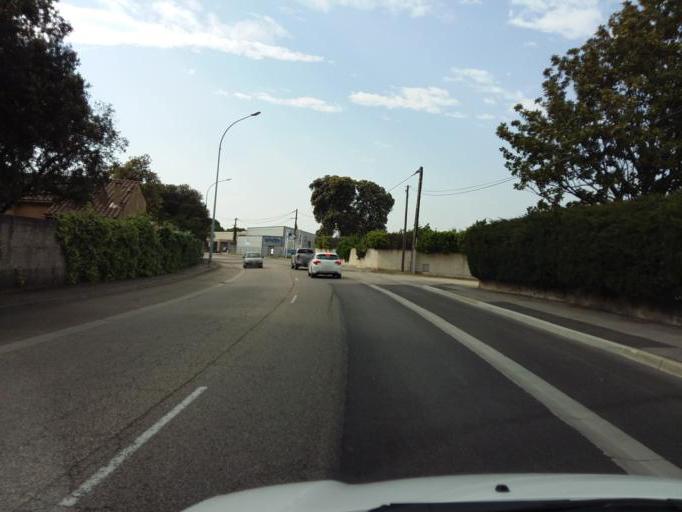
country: FR
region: Provence-Alpes-Cote d'Azur
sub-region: Departement du Vaucluse
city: Bollene
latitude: 44.2873
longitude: 4.7587
